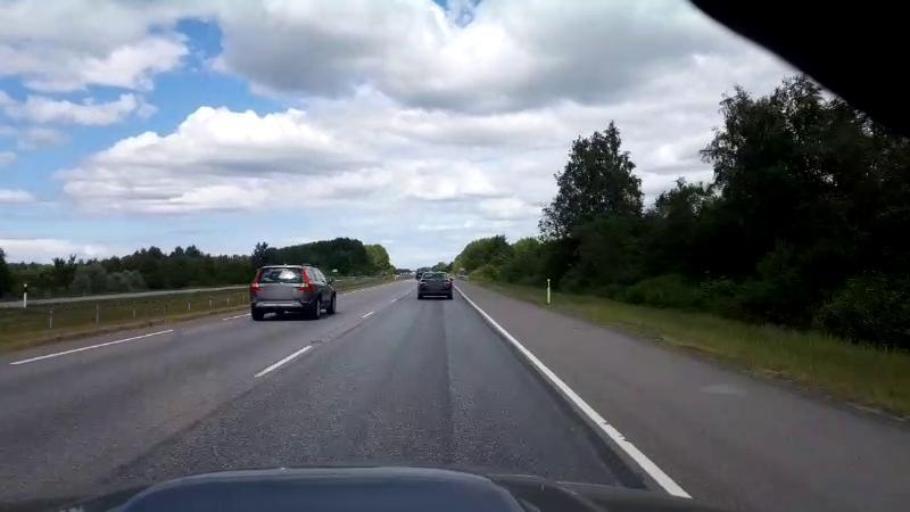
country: EE
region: Harju
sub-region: Saue linn
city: Saue
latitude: 59.2596
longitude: 24.5087
